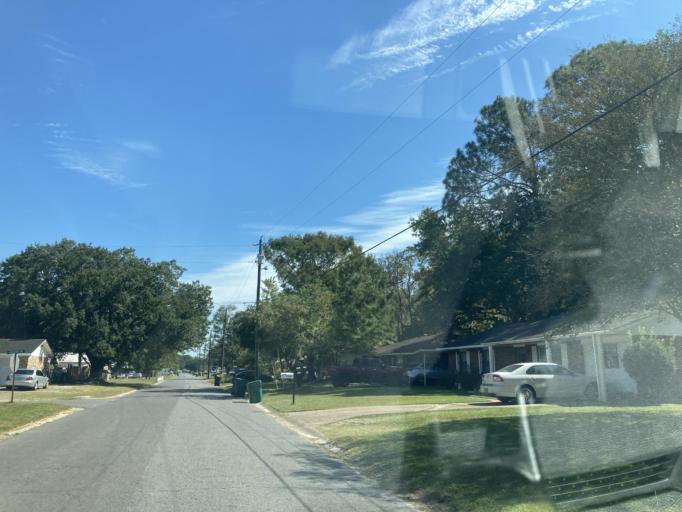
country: US
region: Mississippi
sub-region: Jackson County
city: Saint Martin
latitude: 30.4508
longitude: -88.8736
